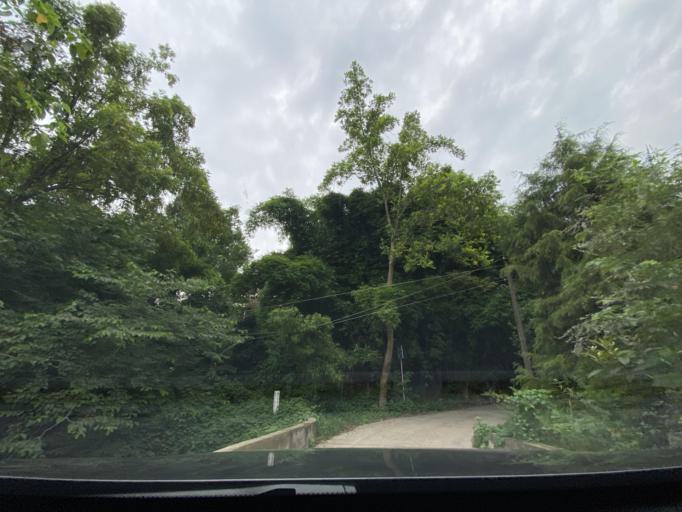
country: CN
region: Sichuan
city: Jiancheng
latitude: 30.3866
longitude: 104.4955
